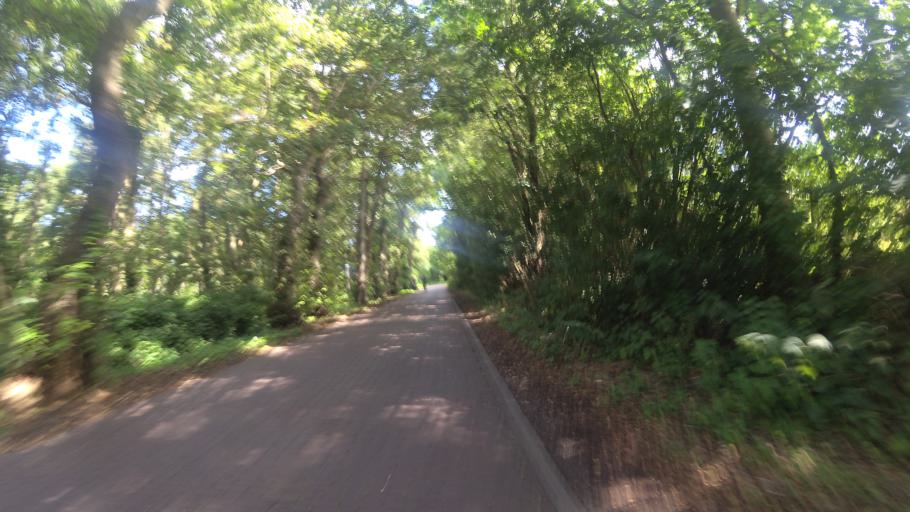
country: NL
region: Zeeland
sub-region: Schouwen-Duiveland
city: Haamstede
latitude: 51.7156
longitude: 3.7543
